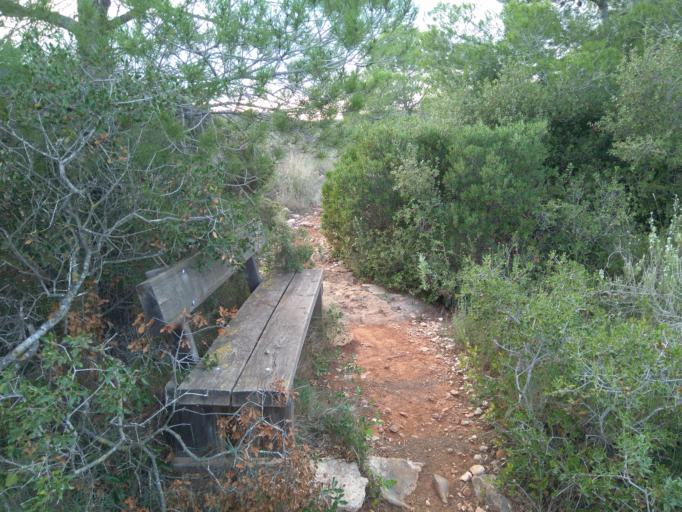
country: ES
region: Valencia
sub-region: Provincia de Valencia
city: Benimodo
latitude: 39.1979
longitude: -0.5784
